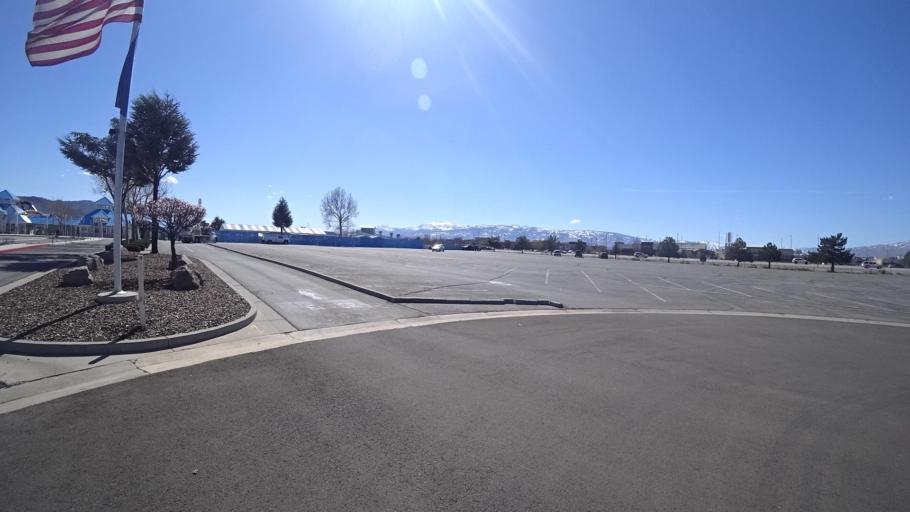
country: US
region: Nevada
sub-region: Washoe County
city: Sparks
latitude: 39.5323
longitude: -119.7138
